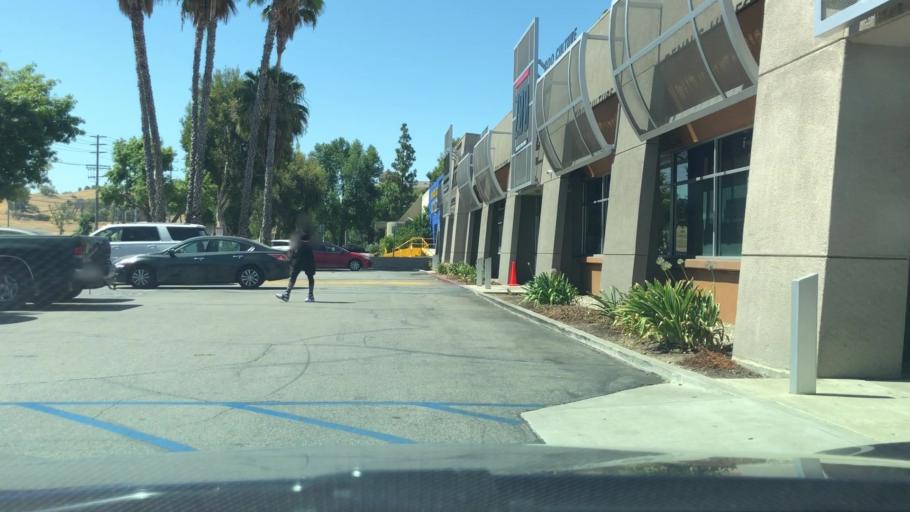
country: US
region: California
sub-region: Los Angeles County
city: Canoga Park
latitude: 34.1878
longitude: -118.5888
